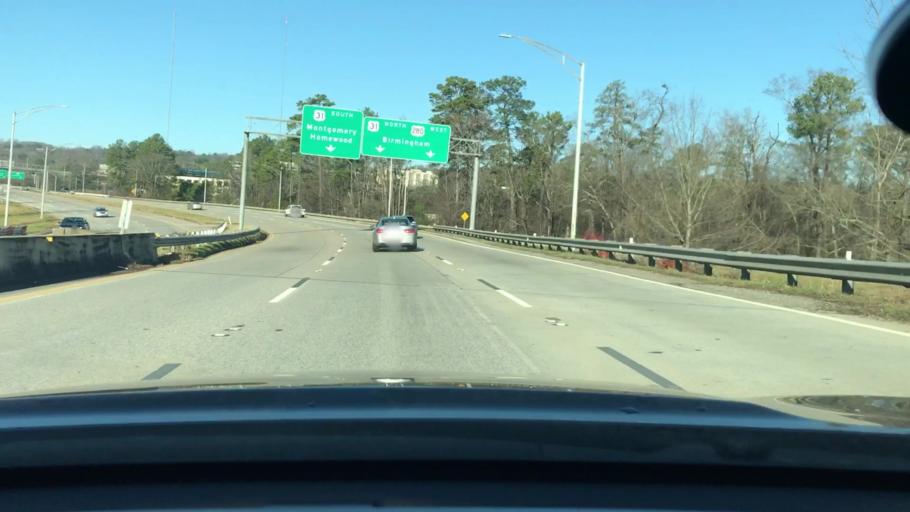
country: US
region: Alabama
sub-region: Jefferson County
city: Homewood
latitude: 33.4833
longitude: -86.7794
